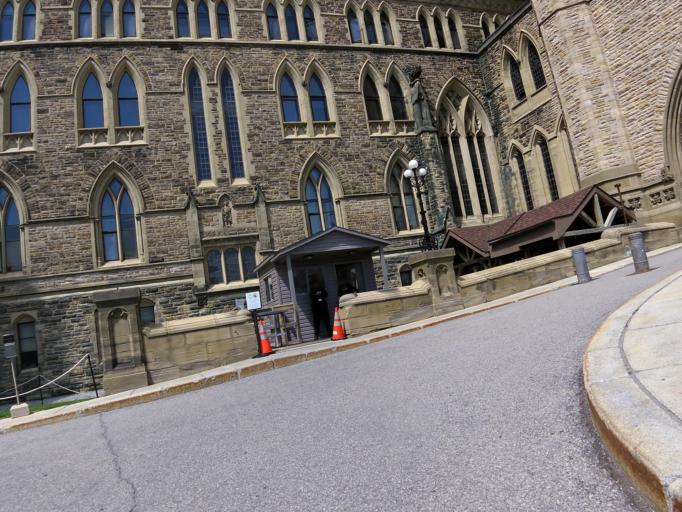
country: CA
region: Ontario
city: Ottawa
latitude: 45.4246
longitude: -75.6999
